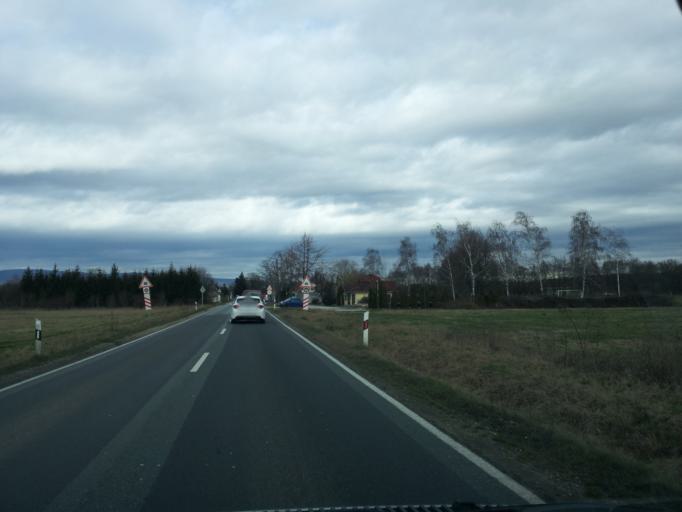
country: HU
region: Vas
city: Gencsapati
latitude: 47.3150
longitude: 16.5906
